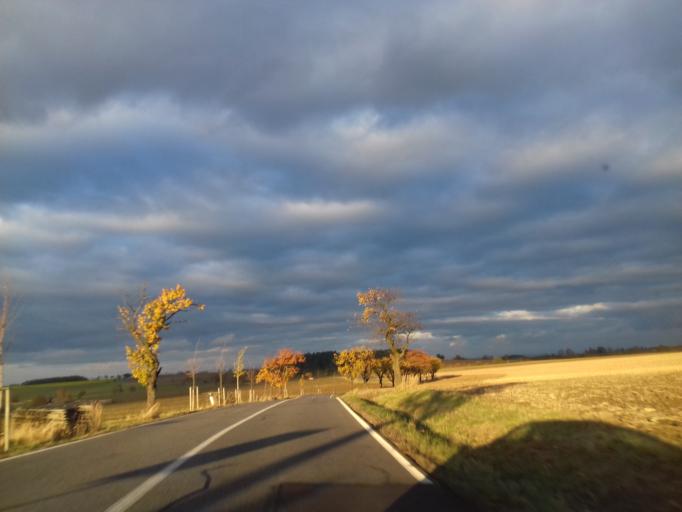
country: CZ
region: Pardubicky
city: Krouna
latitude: 49.7946
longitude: 16.0355
